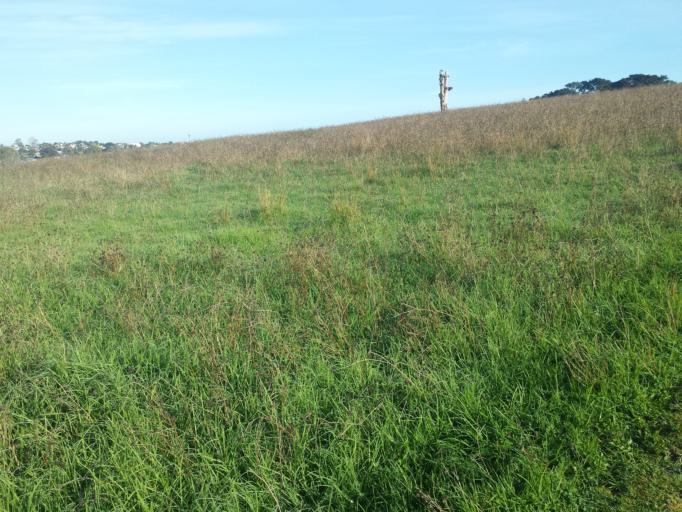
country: NZ
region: Auckland
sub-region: Auckland
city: Tamaki
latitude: -36.8556
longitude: 174.8766
